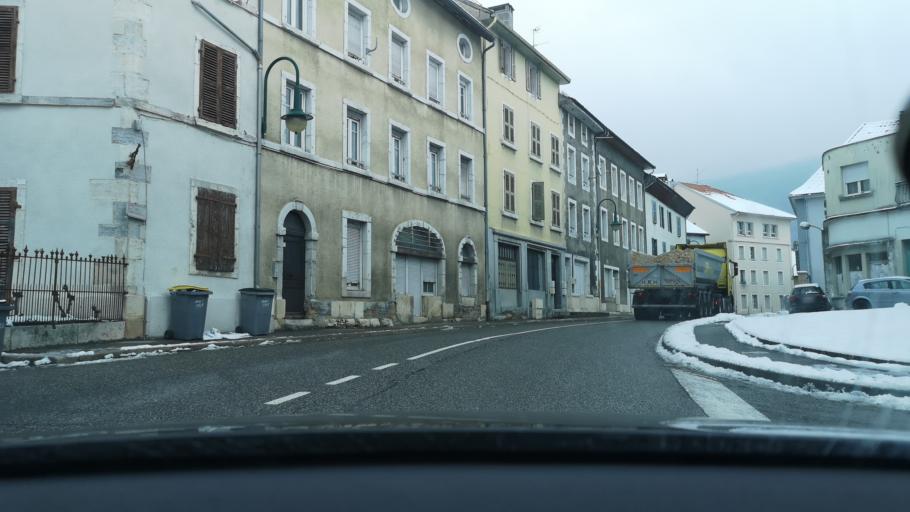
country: FR
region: Rhone-Alpes
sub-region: Departement de l'Ain
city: Chatillon-en-Michaille
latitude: 46.1447
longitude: 5.7992
